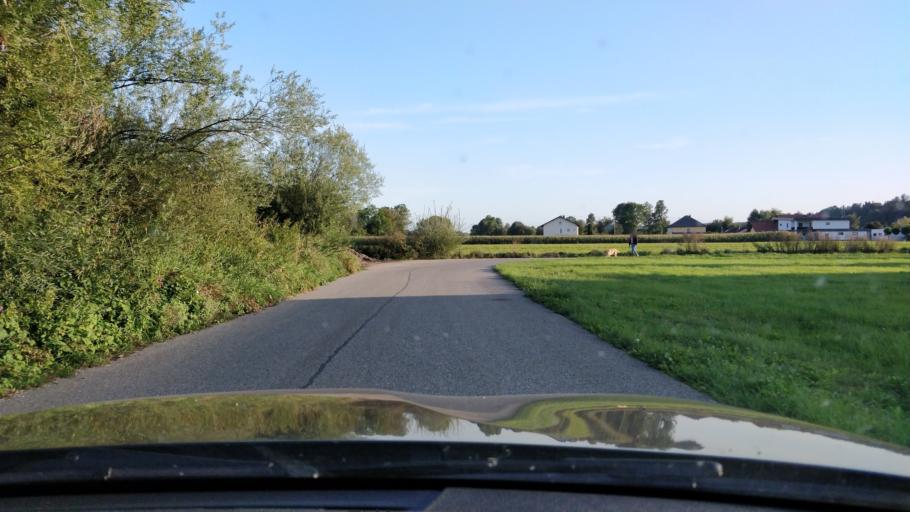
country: AT
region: Upper Austria
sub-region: Politischer Bezirk Braunau am Inn
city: Braunau am Inn
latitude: 48.1682
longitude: 13.1241
